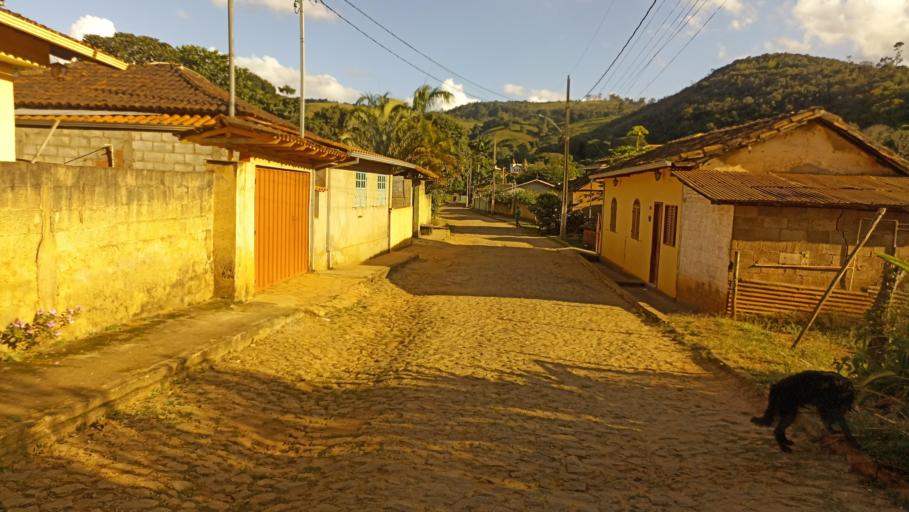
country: BR
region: Minas Gerais
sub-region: Ouro Preto
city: Ouro Preto
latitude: -20.3108
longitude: -43.5787
